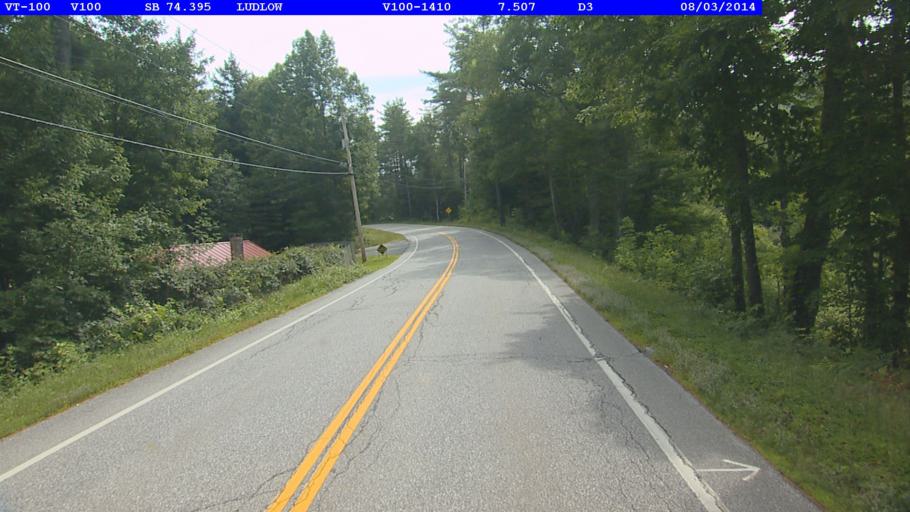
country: US
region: Vermont
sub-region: Windsor County
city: Chester
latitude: 43.4511
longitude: -72.7065
